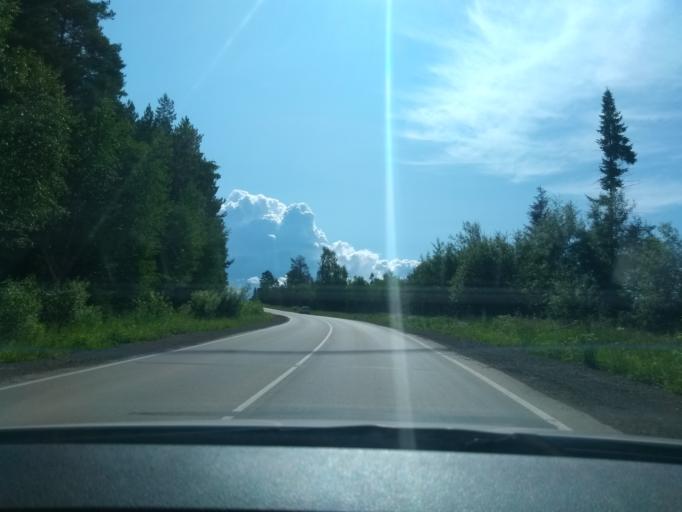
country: RU
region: Perm
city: Bershet'
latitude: 57.8261
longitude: 56.4171
